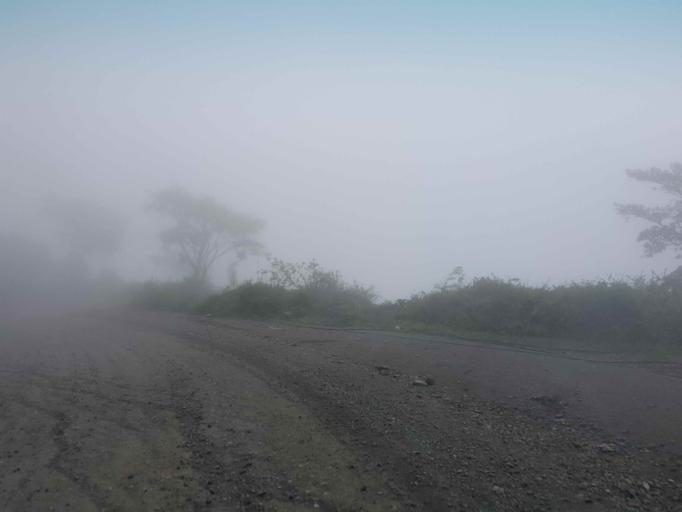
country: CR
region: Guanacaste
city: Juntas
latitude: 10.2984
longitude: -84.8350
